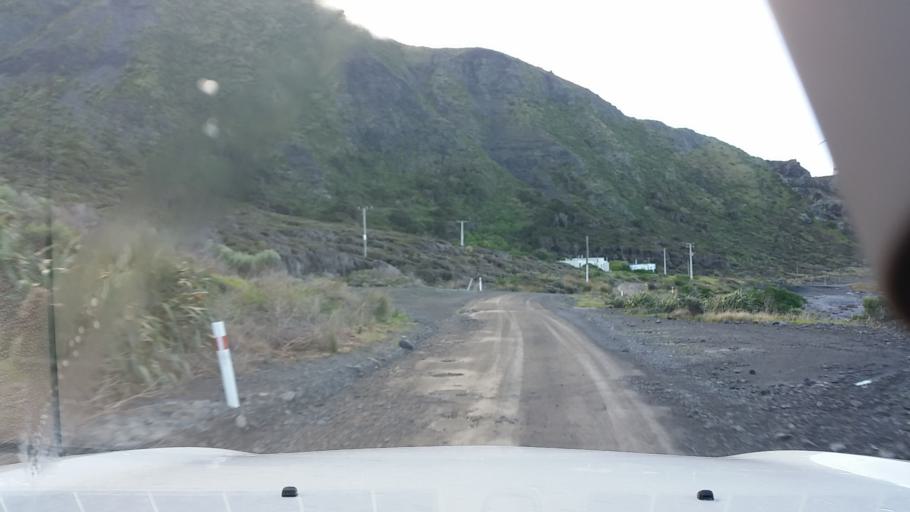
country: NZ
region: Wellington
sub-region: South Wairarapa District
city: Waipawa
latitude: -41.6106
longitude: 175.2843
